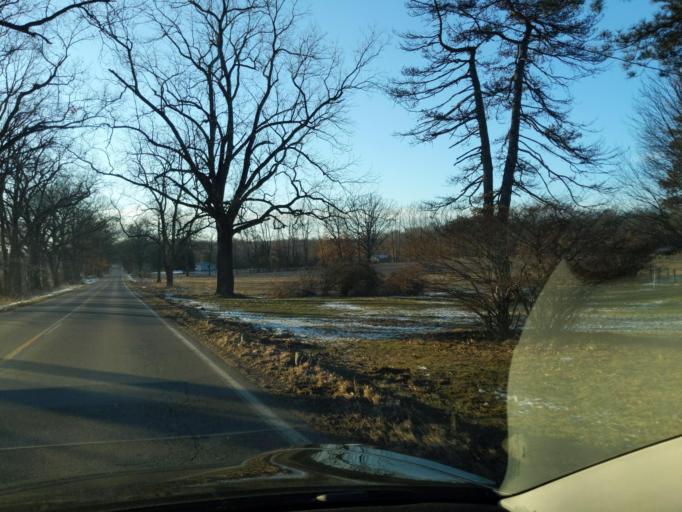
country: US
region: Michigan
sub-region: Ingham County
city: Stockbridge
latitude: 42.4679
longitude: -84.0980
